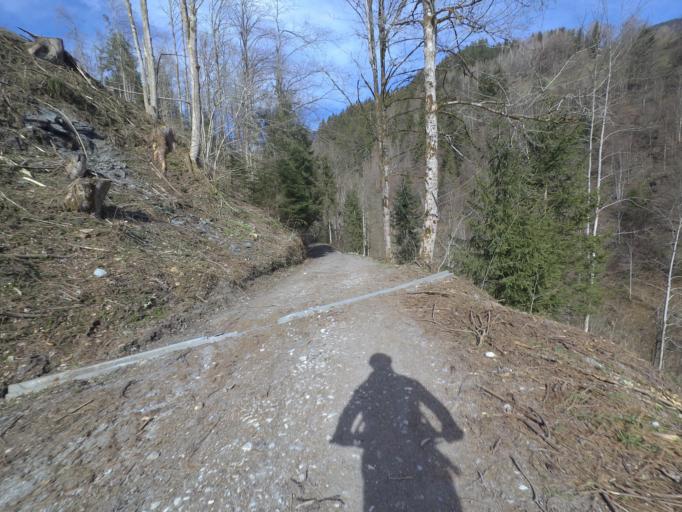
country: AT
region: Salzburg
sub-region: Politischer Bezirk Sankt Johann im Pongau
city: Sankt Veit im Pongau
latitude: 47.3282
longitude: 13.1345
